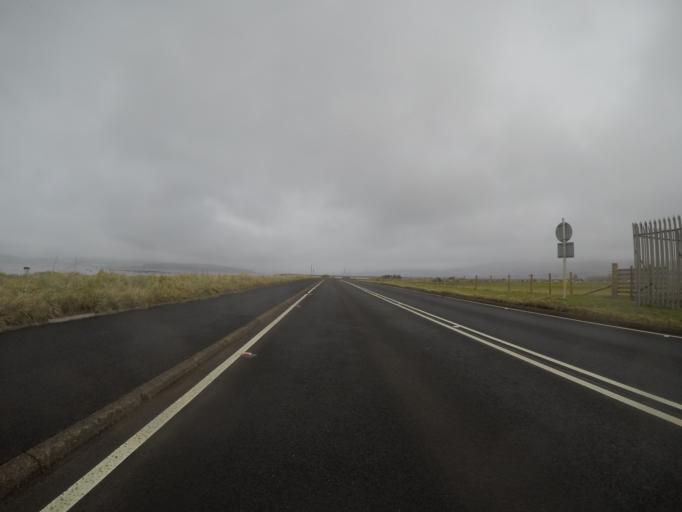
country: GB
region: Scotland
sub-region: North Ayrshire
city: Millport
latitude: 55.7243
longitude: -4.8982
